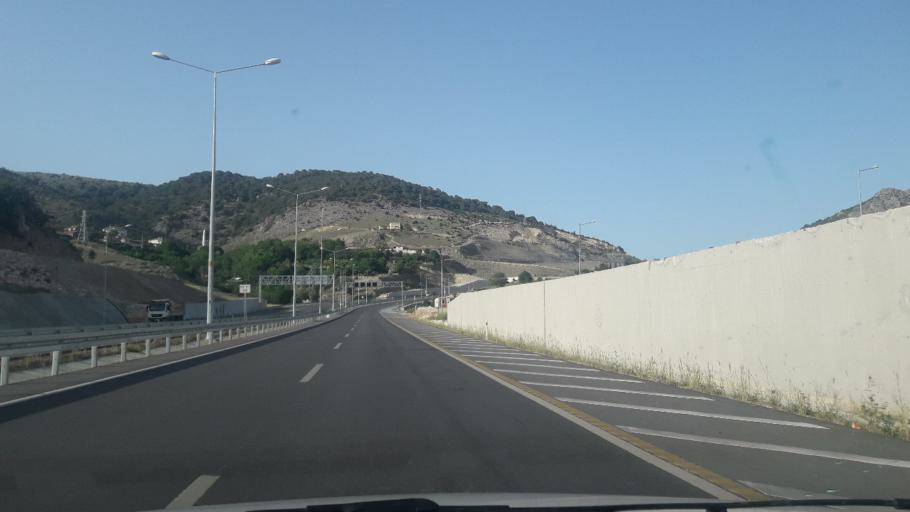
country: TR
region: Amasya
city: Amasya
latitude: 40.6598
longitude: 35.7881
